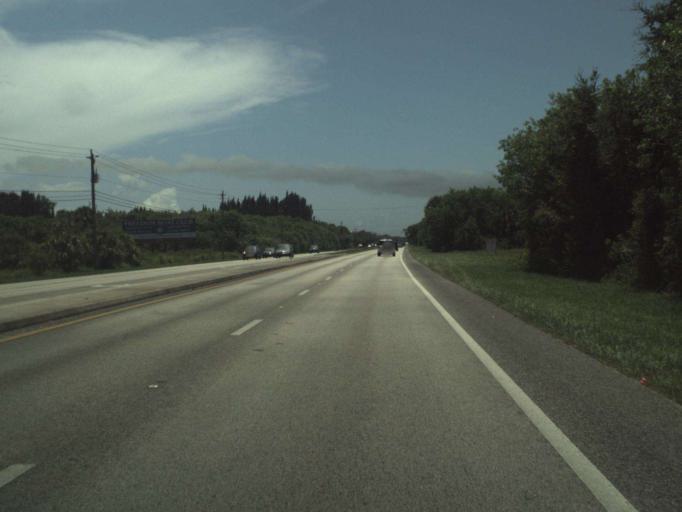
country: US
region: Florida
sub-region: Indian River County
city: Winter Beach
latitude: 27.7261
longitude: -80.4235
